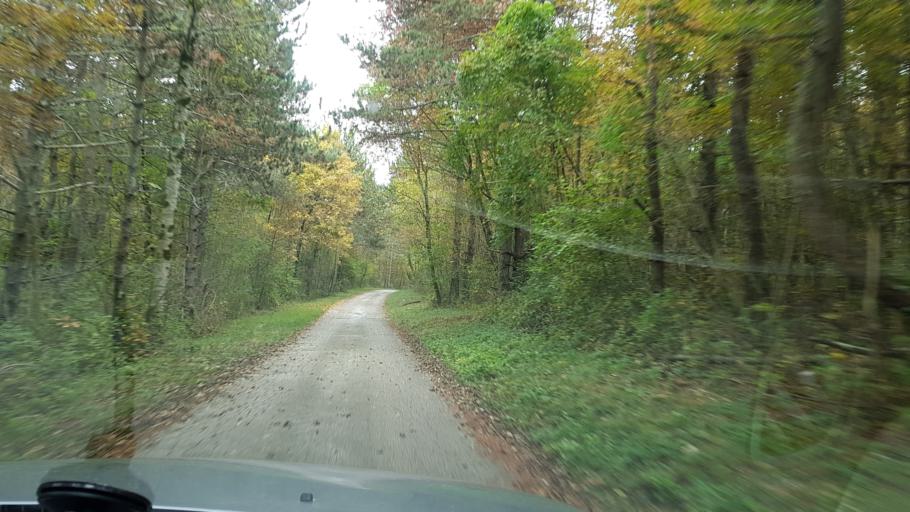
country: HR
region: Istarska
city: Buzet
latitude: 45.4469
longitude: 14.0362
